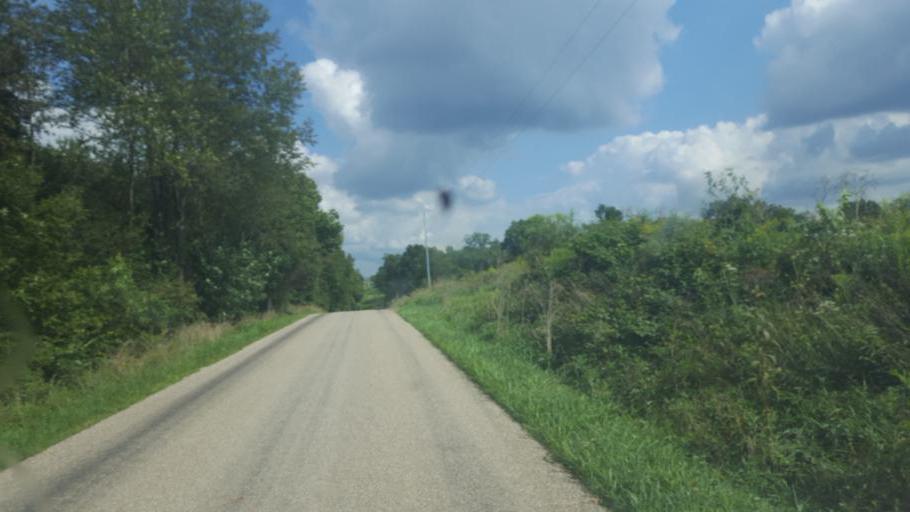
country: US
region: Ohio
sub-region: Knox County
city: Oak Hill
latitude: 40.3816
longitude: -82.2926
